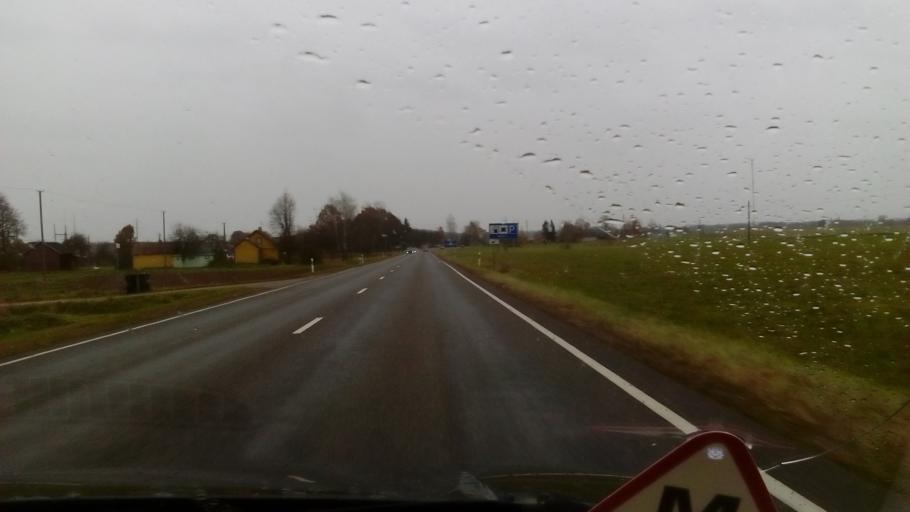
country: LT
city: Simnas
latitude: 54.5606
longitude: 23.6434
